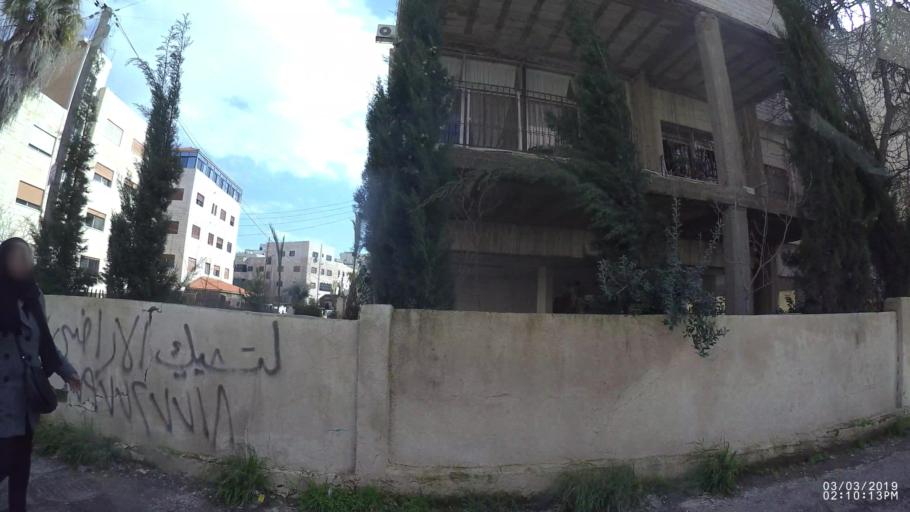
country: JO
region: Amman
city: Al Jubayhah
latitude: 31.9766
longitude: 35.8890
